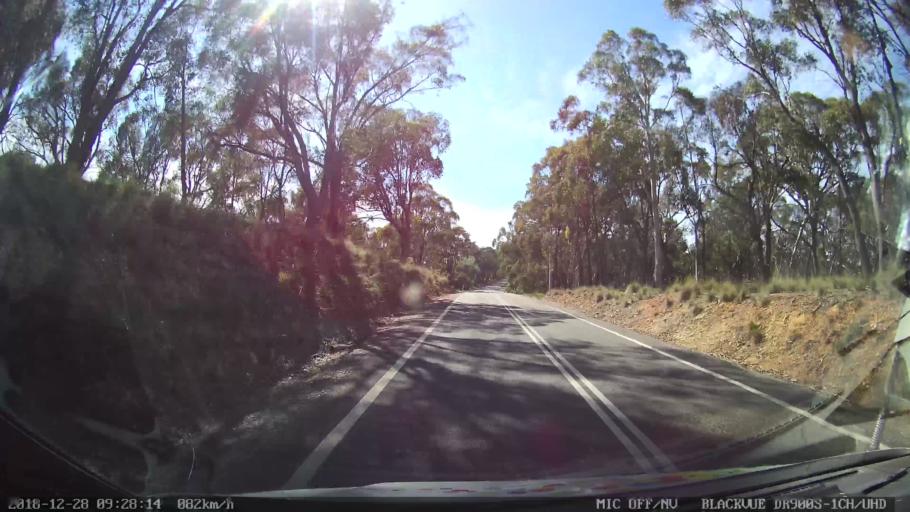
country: AU
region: New South Wales
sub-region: Upper Lachlan Shire
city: Crookwell
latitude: -34.4374
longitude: 149.4136
